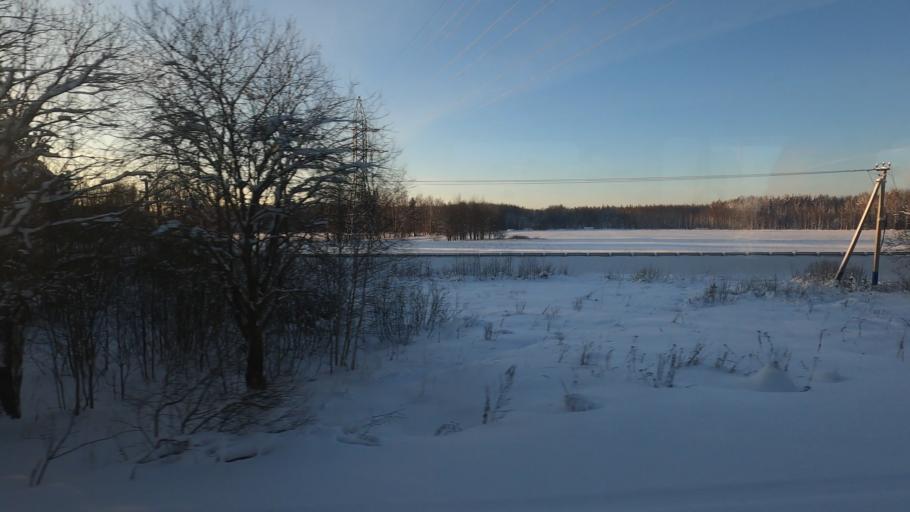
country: RU
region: Moskovskaya
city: Novo-Nikol'skoye
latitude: 56.6441
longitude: 37.5625
